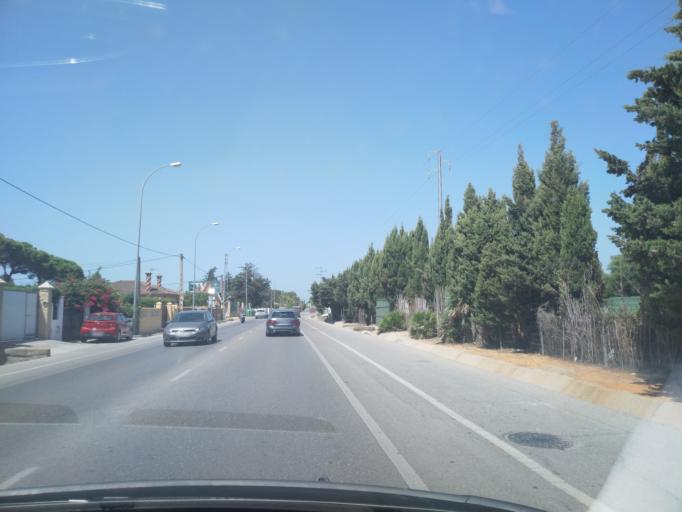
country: ES
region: Andalusia
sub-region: Provincia de Cadiz
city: Chiclana de la Frontera
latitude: 36.3947
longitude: -6.1578
